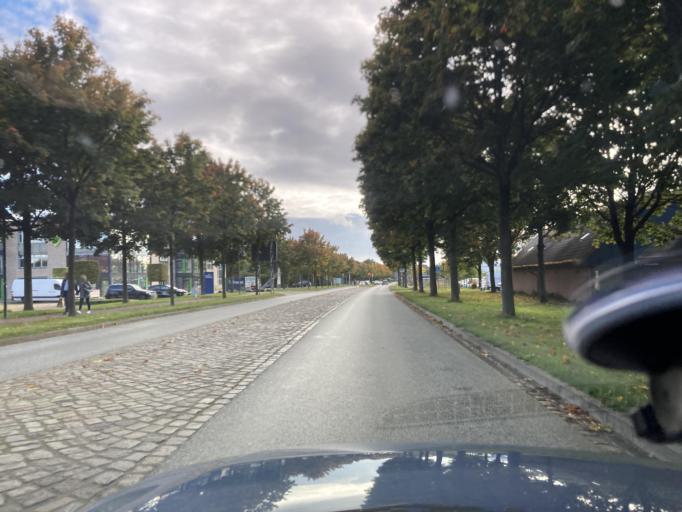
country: DE
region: Schleswig-Holstein
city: Budelsdorf
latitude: 54.3243
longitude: 9.6944
